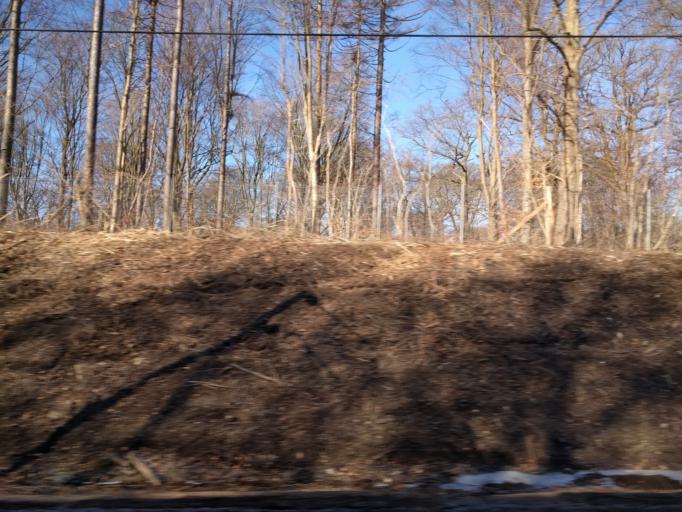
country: DK
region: Capital Region
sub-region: Gentofte Kommune
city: Charlottenlund
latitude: 55.7785
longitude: 12.5850
